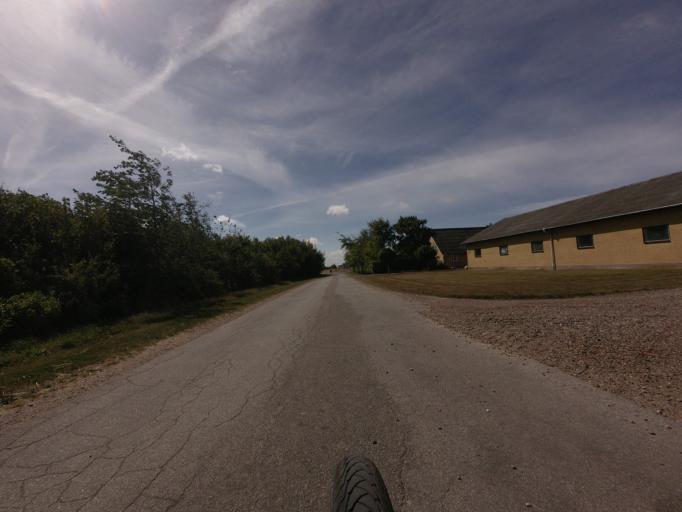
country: DK
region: North Denmark
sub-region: Hjorring Kommune
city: Vra
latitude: 57.3335
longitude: 9.8090
